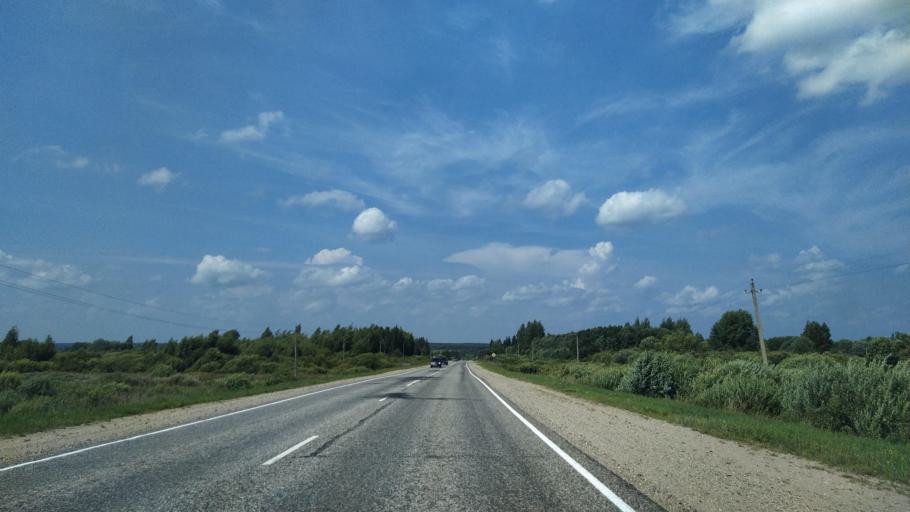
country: RU
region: Pskov
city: Pushkinskiye Gory
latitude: 57.0166
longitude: 28.8842
